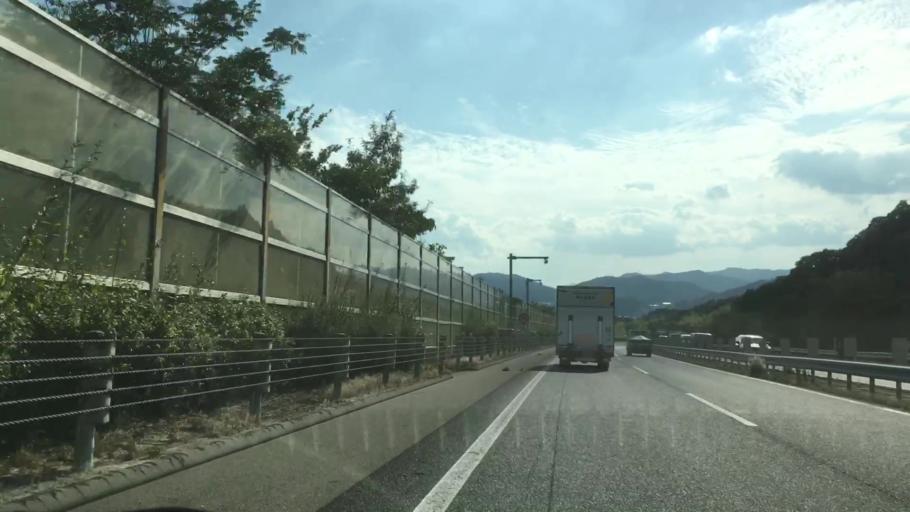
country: JP
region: Hiroshima
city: Ono-hara
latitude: 34.2681
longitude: 132.2428
